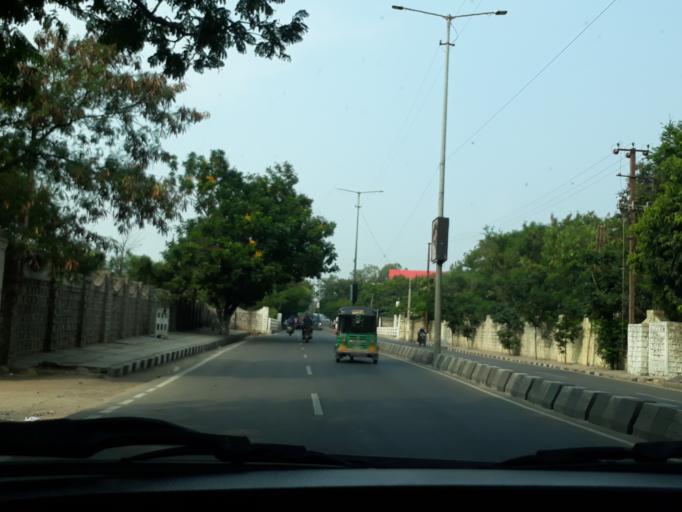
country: IN
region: Telangana
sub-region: Hyderabad
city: Malkajgiri
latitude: 17.4456
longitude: 78.4914
